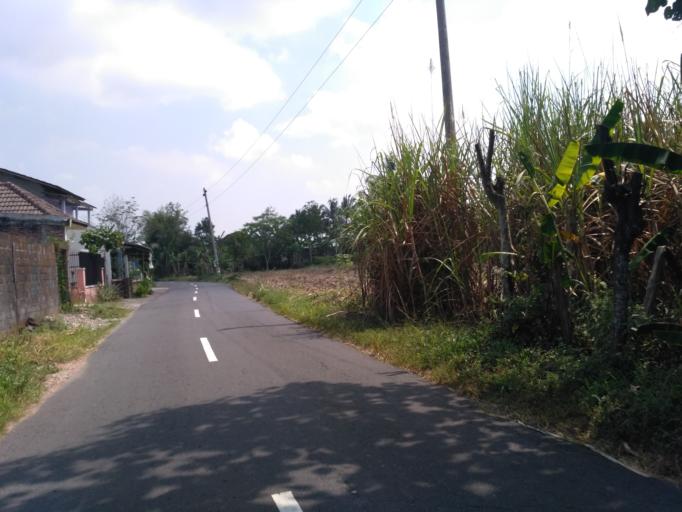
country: ID
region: Daerah Istimewa Yogyakarta
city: Depok
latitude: -7.7190
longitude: 110.4225
